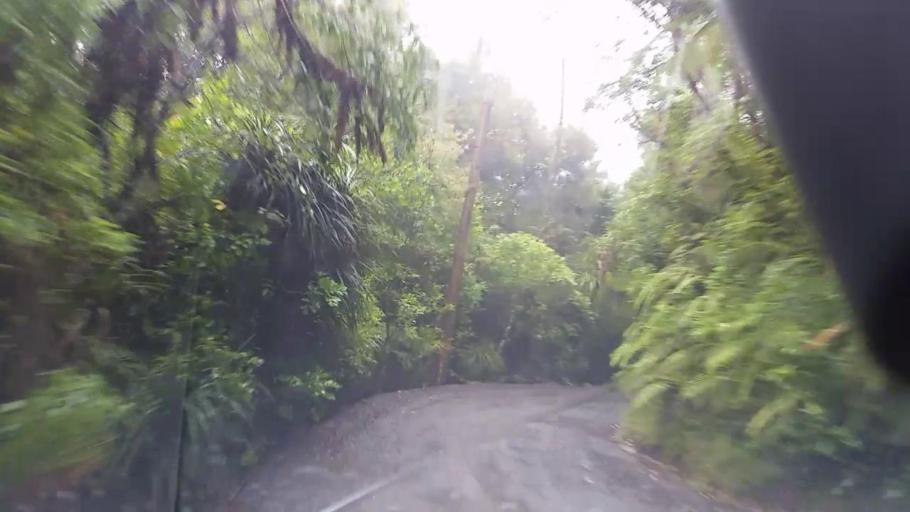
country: NZ
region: Auckland
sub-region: Auckland
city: Titirangi
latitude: -36.9198
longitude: 174.5619
